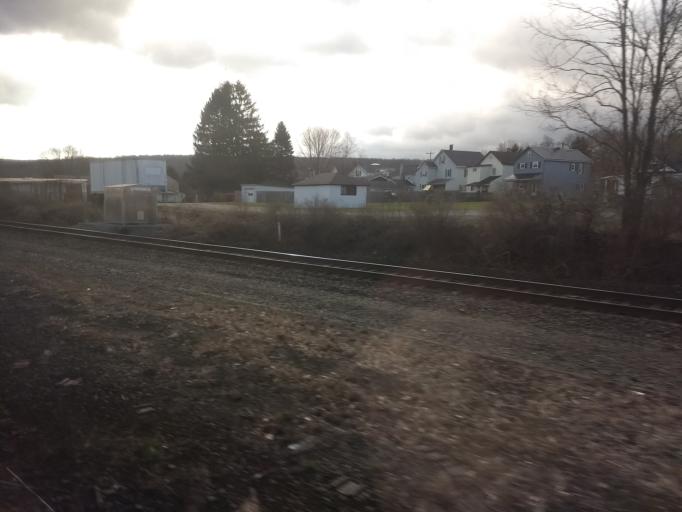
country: US
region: Pennsylvania
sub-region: Cambria County
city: Portage
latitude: 40.3900
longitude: -78.6750
